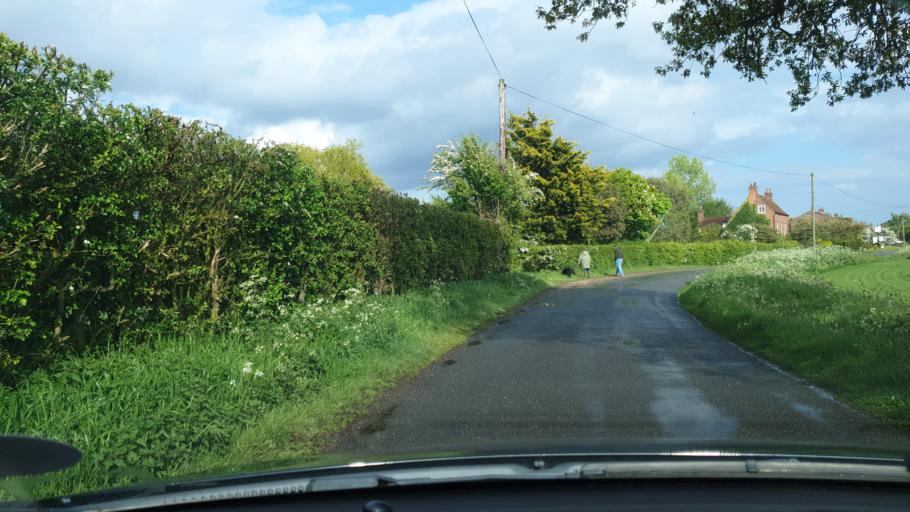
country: GB
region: England
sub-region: Essex
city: Saint Osyth
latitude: 51.8247
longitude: 1.1000
